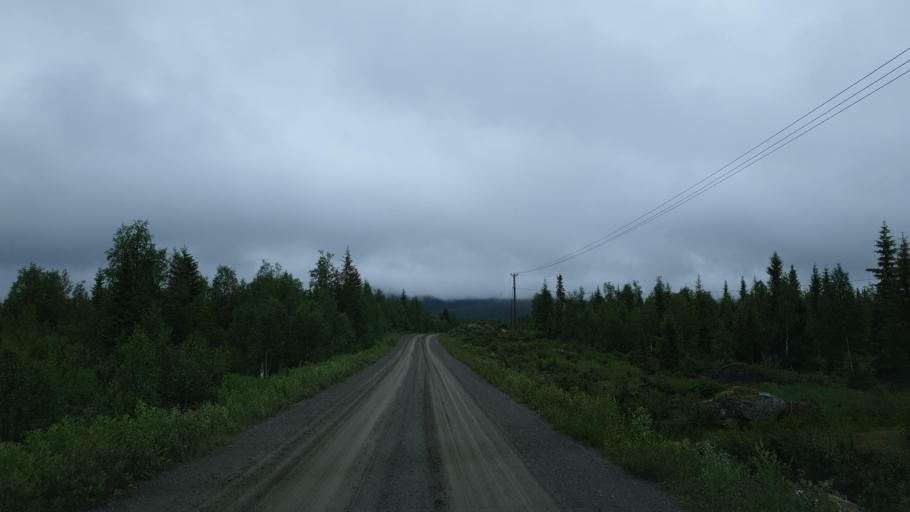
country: SE
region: Vaesterbotten
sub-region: Vilhelmina Kommun
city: Sjoberg
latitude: 65.3109
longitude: 16.0203
